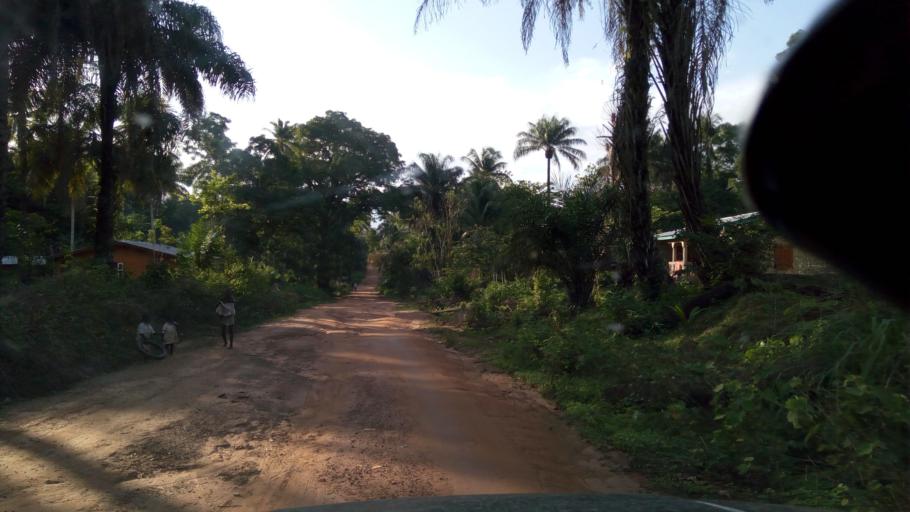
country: SL
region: Northern Province
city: Konakridee
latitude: 8.7317
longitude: -13.1443
